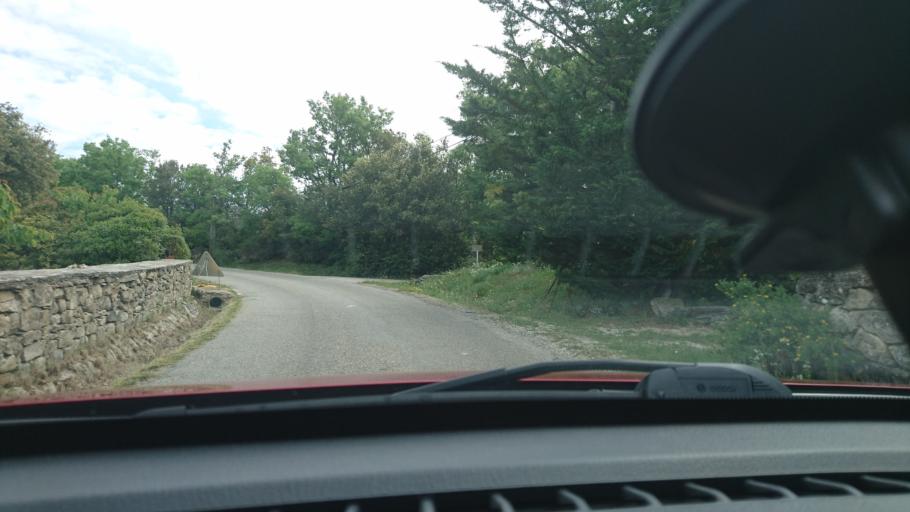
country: FR
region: Provence-Alpes-Cote d'Azur
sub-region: Departement du Vaucluse
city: Gordes
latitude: 43.9620
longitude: 5.2490
